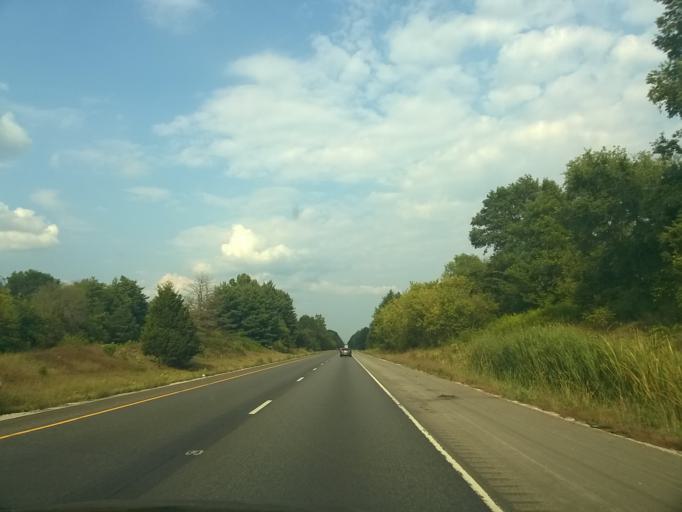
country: US
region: Indiana
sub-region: Clay County
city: Brazil
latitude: 39.4513
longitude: -87.1069
